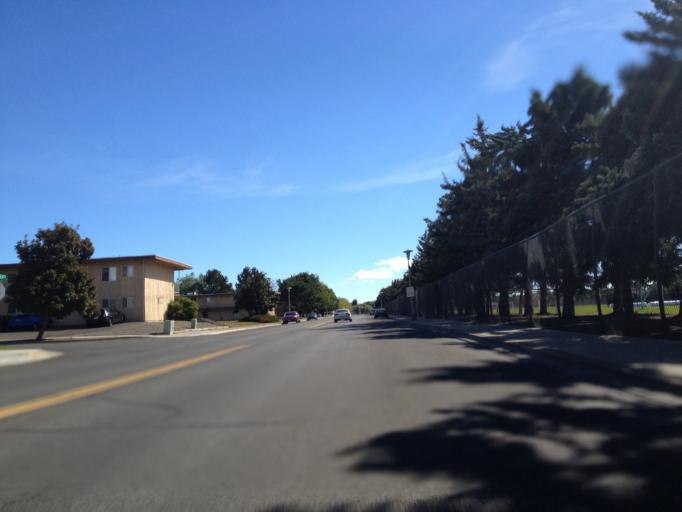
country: US
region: Washington
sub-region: Kittitas County
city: Ellensburg
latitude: 47.0103
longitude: -120.5376
